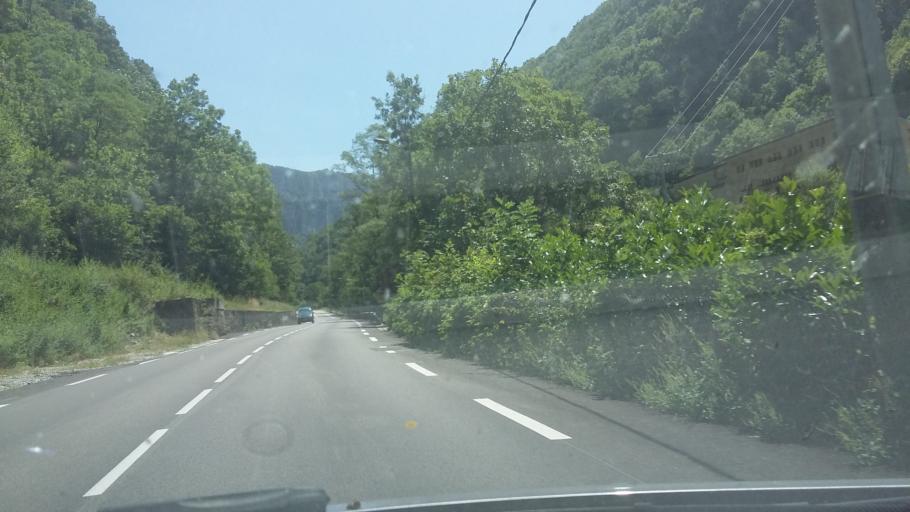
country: FR
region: Rhone-Alpes
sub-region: Departement de l'Ain
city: Tenay
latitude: 45.9251
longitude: 5.4995
